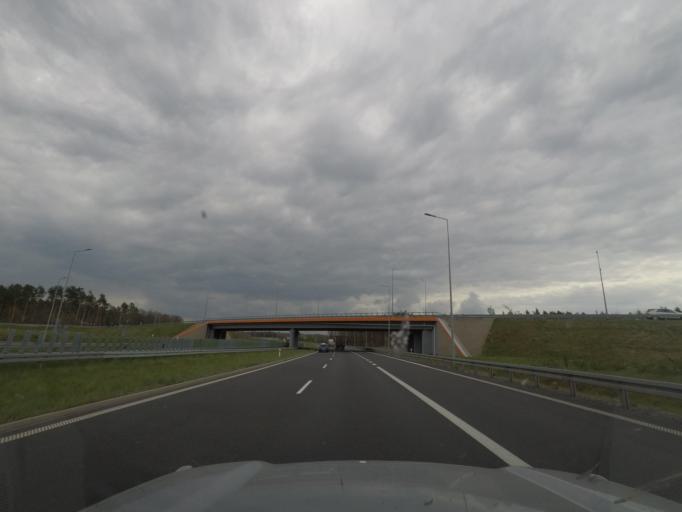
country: PL
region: Lubusz
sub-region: Powiat nowosolski
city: Nowe Miasteczko
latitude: 51.6830
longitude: 15.7605
